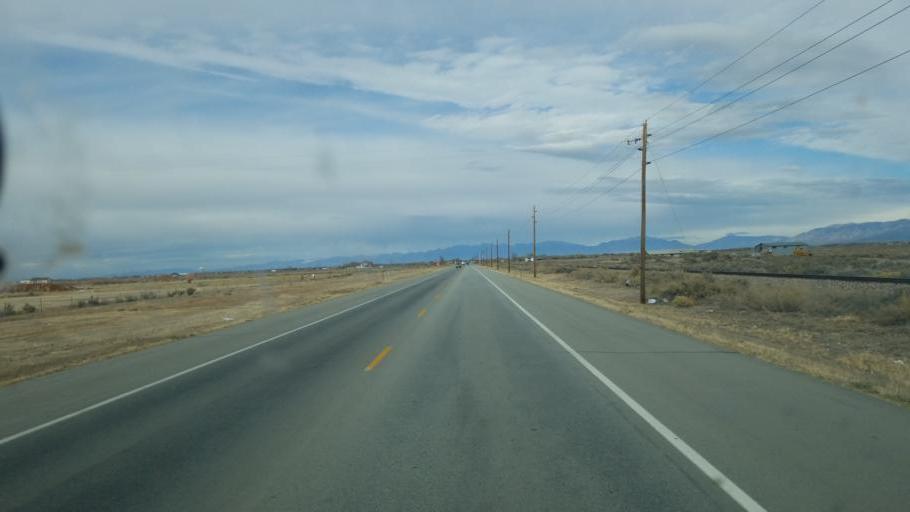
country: US
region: Colorado
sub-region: Alamosa County
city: Alamosa
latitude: 37.4189
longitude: -105.8967
